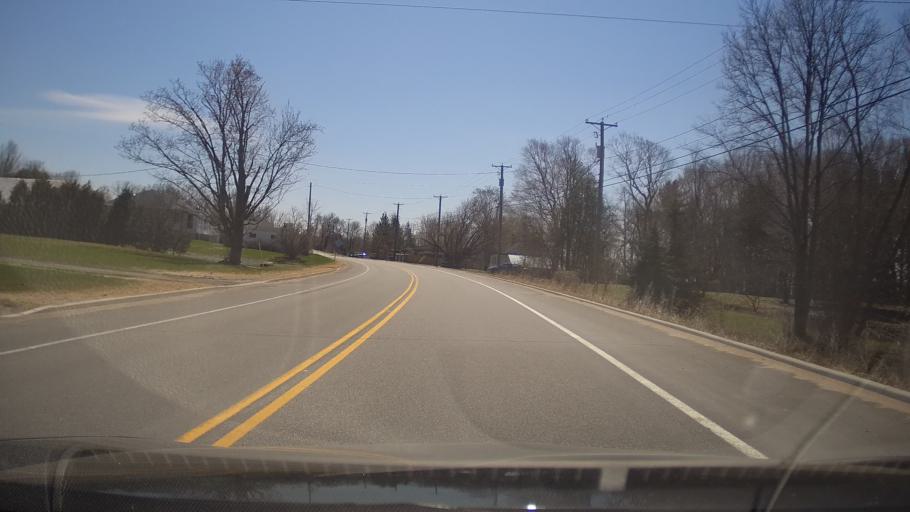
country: CA
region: Ontario
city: Bells Corners
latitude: 45.4436
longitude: -75.9192
